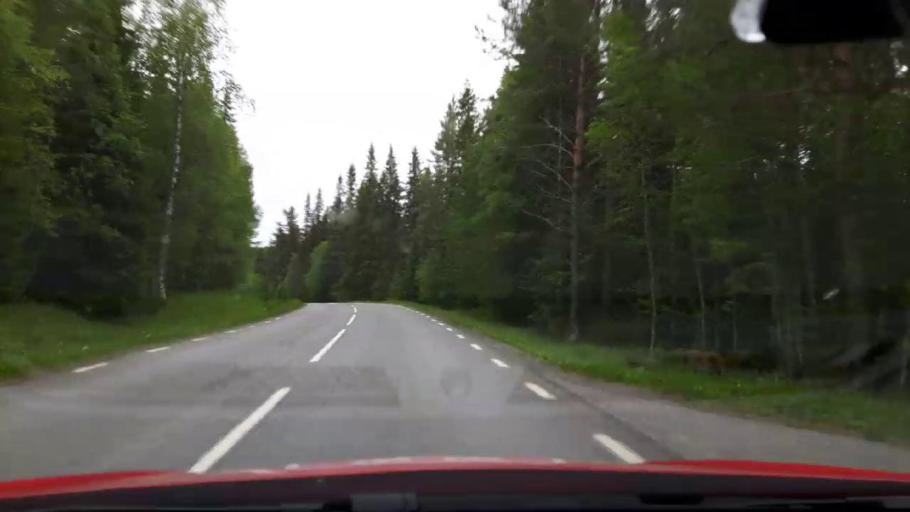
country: SE
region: Jaemtland
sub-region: Stroemsunds Kommun
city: Stroemsund
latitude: 63.4484
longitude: 15.4706
